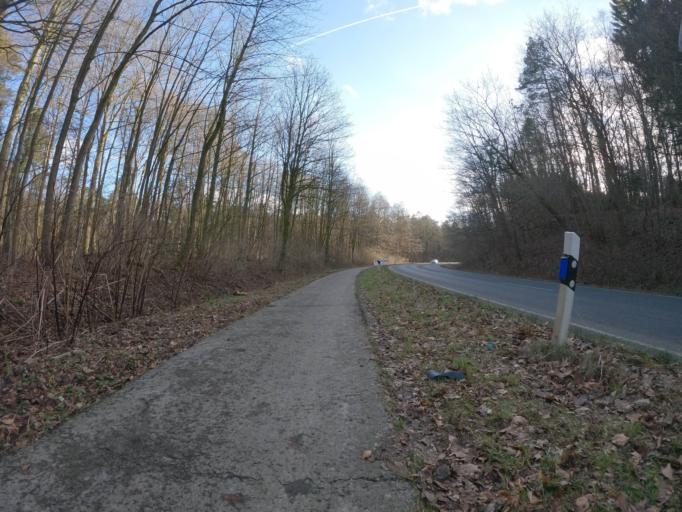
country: DE
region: North Rhine-Westphalia
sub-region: Regierungsbezirk Koln
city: Aachen
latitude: 50.7311
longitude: 6.0922
